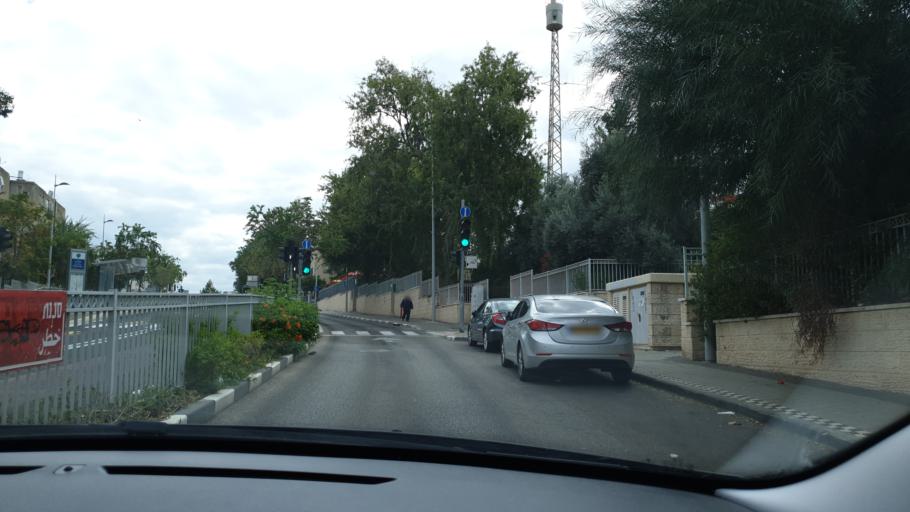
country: IL
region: Haifa
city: Qiryat Ata
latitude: 32.8111
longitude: 35.1147
